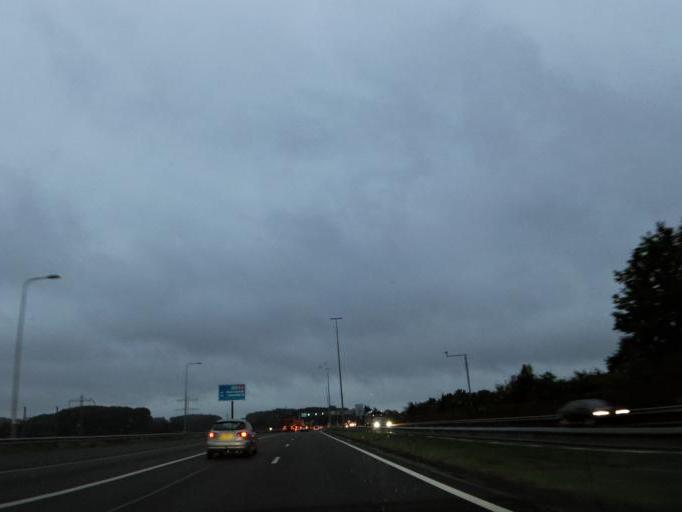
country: NL
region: Limburg
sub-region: Gemeente Sittard-Geleen
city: Born
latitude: 51.0480
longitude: 5.8269
